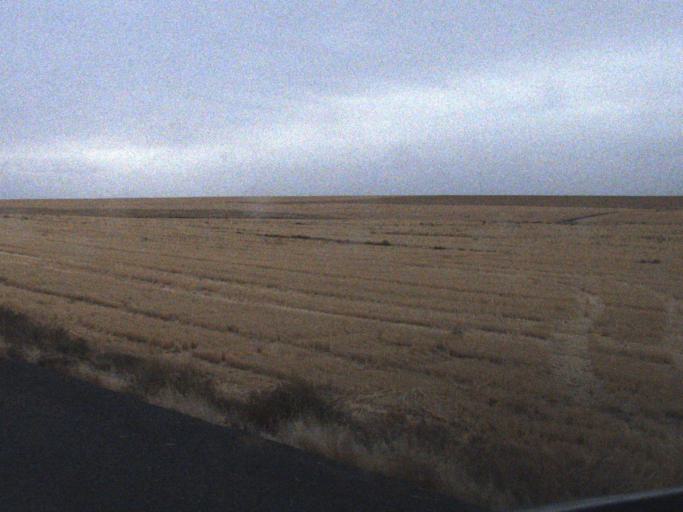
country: US
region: Washington
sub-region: Franklin County
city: Connell
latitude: 46.7944
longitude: -118.6979
